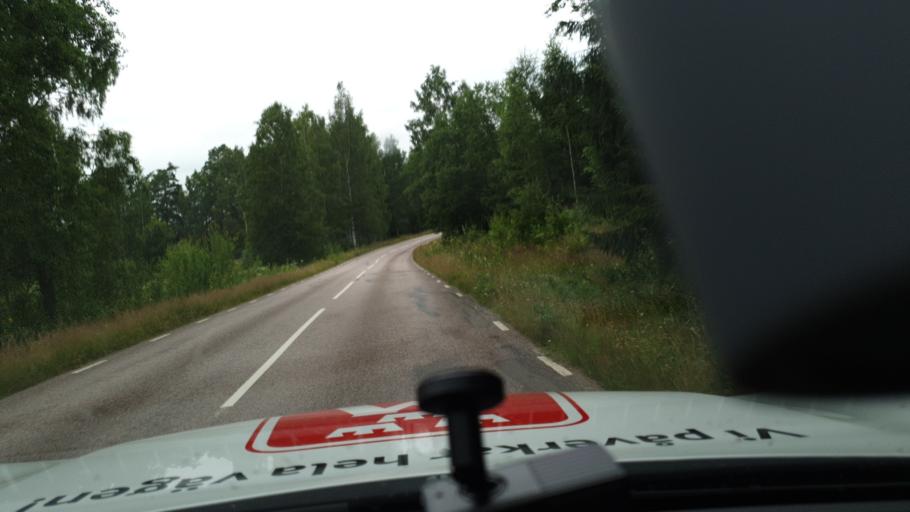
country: SE
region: Vaermland
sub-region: Sunne Kommun
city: Sunne
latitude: 59.7766
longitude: 13.2359
